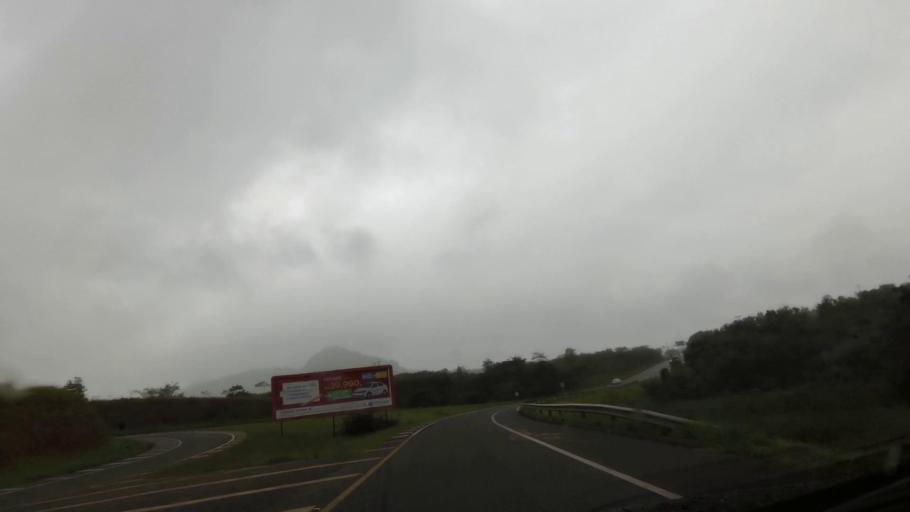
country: BR
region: Espirito Santo
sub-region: Guarapari
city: Guarapari
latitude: -20.6334
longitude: -40.5233
